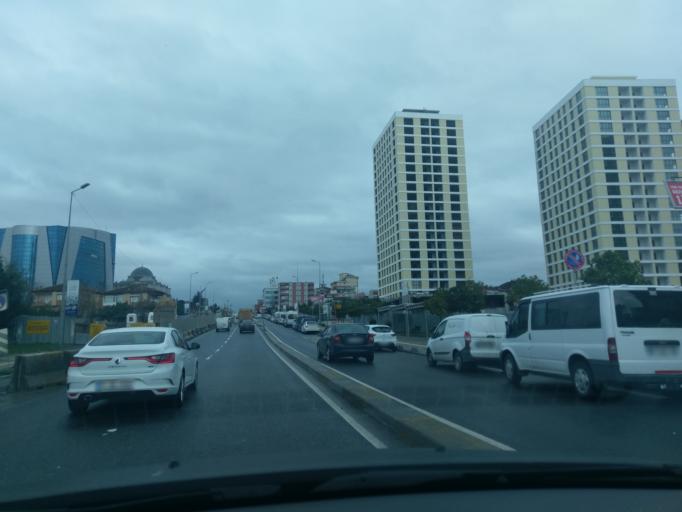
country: TR
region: Istanbul
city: Mahmutbey
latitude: 41.0545
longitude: 28.8304
